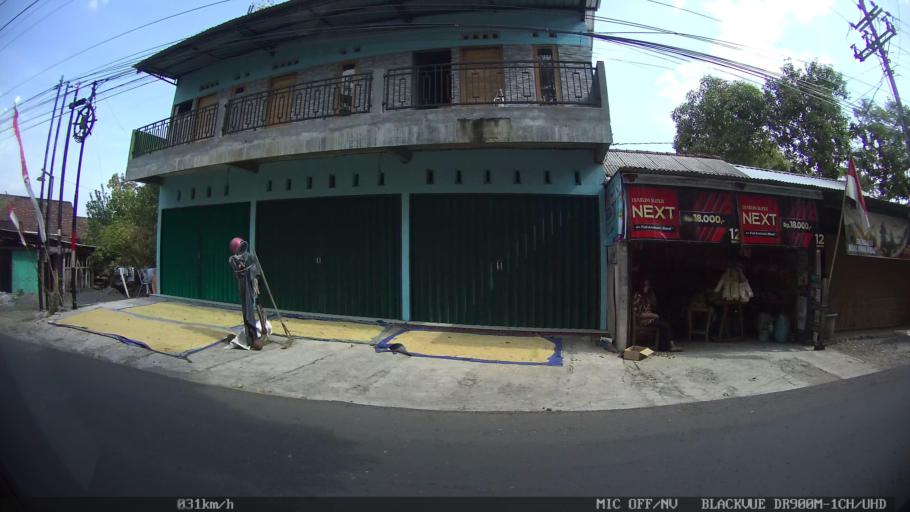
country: ID
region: Daerah Istimewa Yogyakarta
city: Kasihan
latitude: -7.8398
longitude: 110.3230
